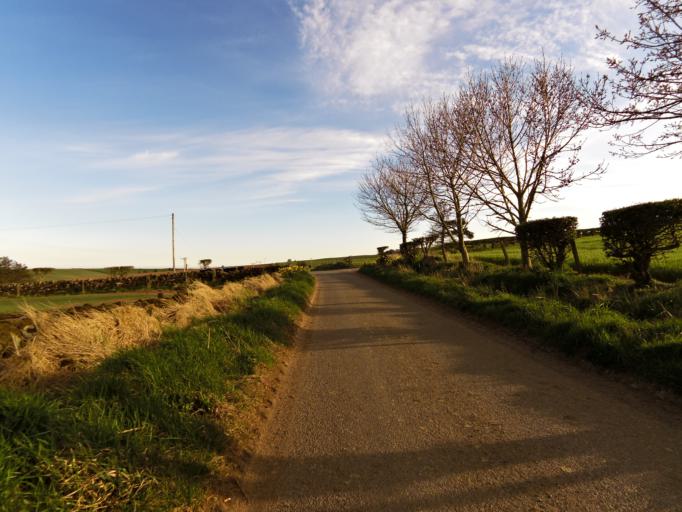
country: GB
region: Scotland
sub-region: Aberdeenshire
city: Inverbervie
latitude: 56.8865
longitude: -2.2375
